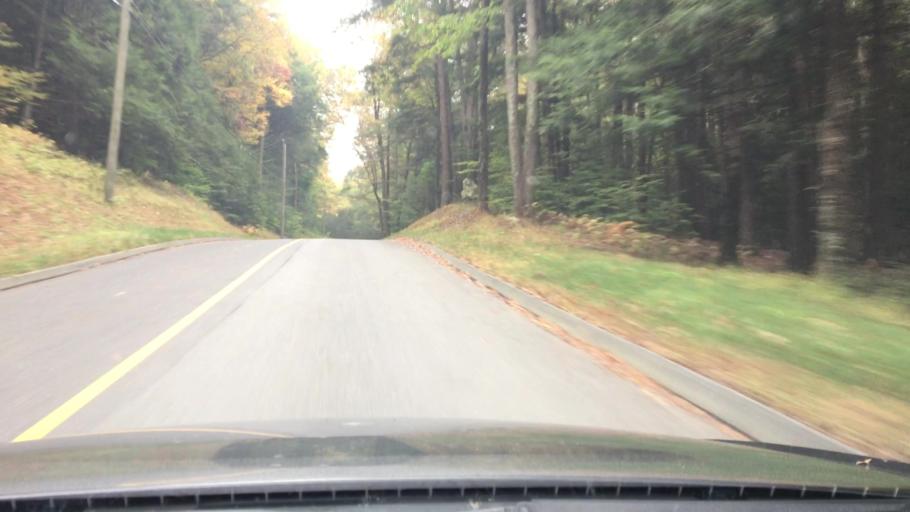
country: US
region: Connecticut
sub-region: New Haven County
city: Heritage Village
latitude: 41.5075
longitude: -73.2697
